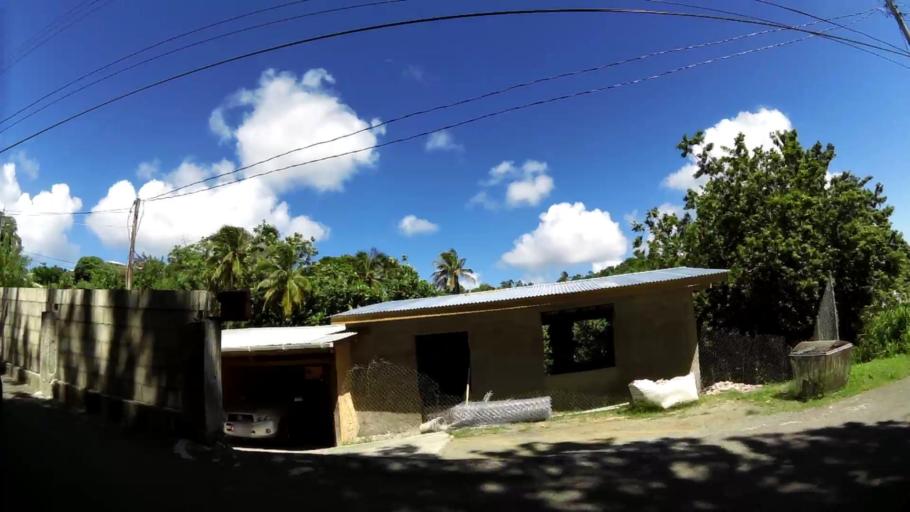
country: TT
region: Tobago
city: Scarborough
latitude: 11.1805
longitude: -60.7822
